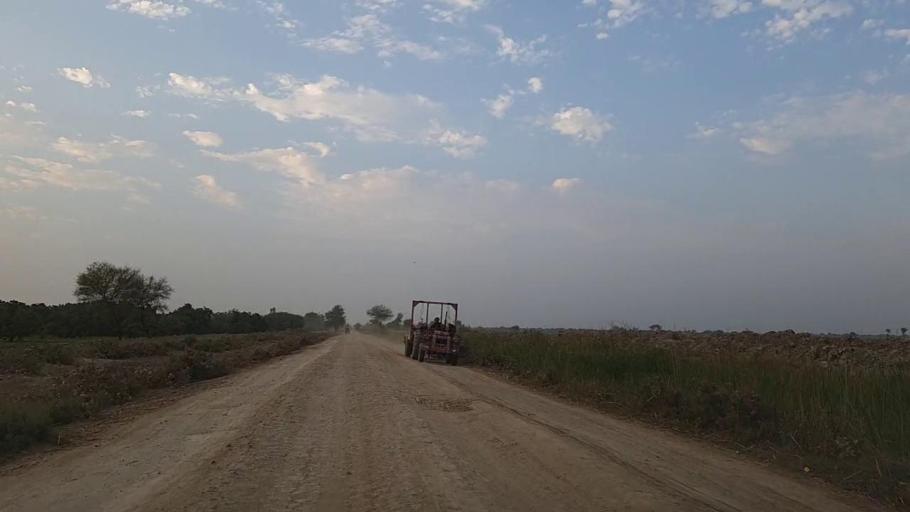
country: PK
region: Sindh
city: Mirwah Gorchani
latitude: 25.3307
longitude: 69.2134
